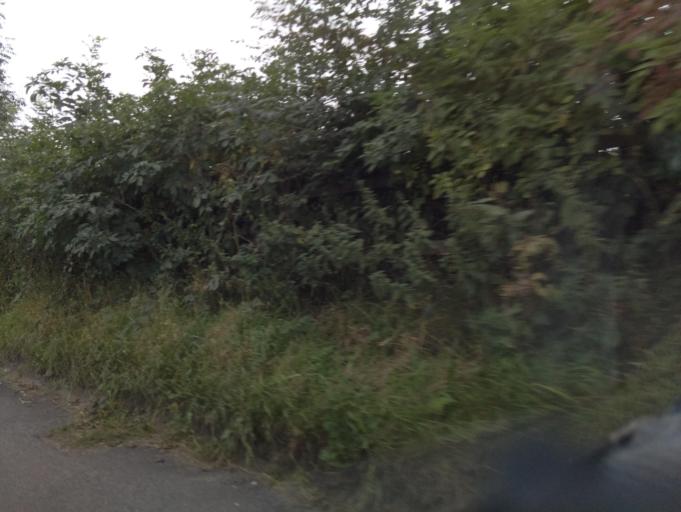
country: GB
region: England
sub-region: Staffordshire
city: Cheadle
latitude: 53.0202
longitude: -1.9910
